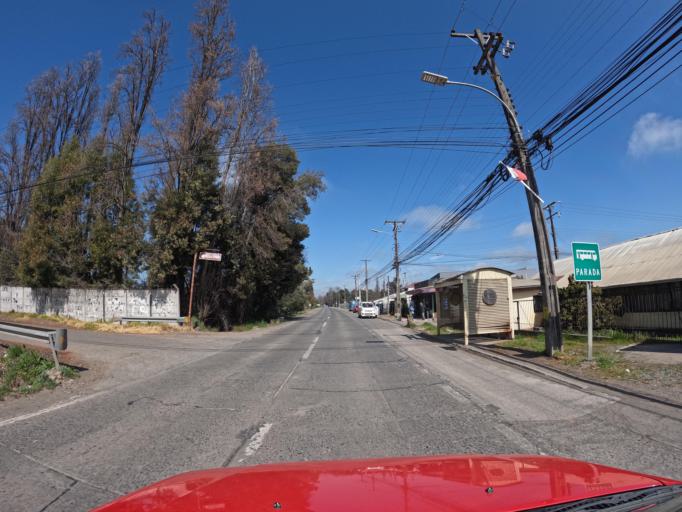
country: CL
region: Maule
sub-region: Provincia de Curico
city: Molina
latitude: -35.0826
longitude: -71.2636
